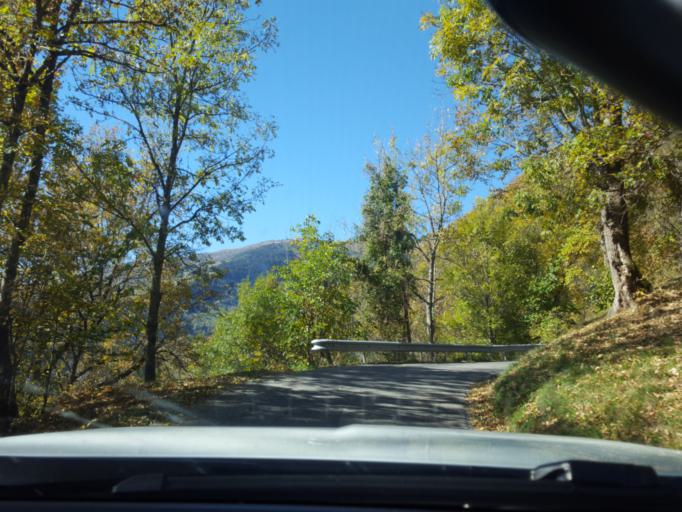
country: FR
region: Rhone-Alpes
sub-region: Departement de la Savoie
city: Bourg-Saint-Maurice
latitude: 45.6277
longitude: 6.7696
